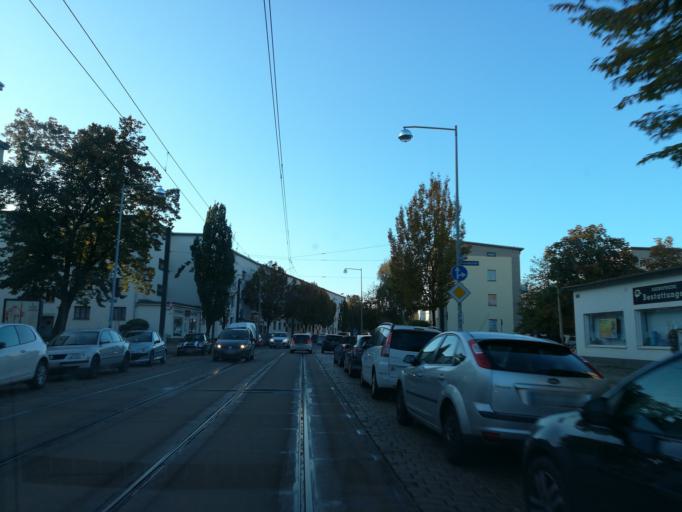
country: DE
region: Saxony-Anhalt
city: Magdeburg
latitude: 52.1221
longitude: 11.6563
